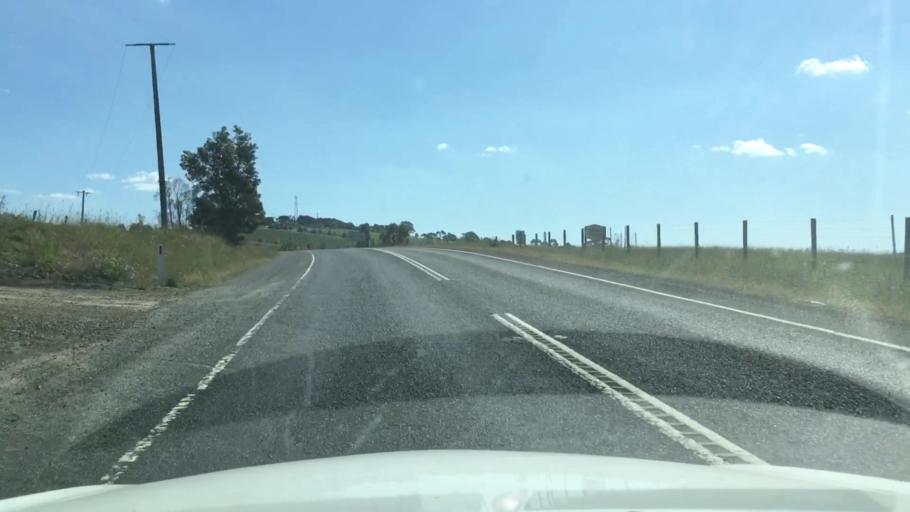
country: AU
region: Victoria
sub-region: Nillumbik
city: North Warrandyte
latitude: -37.6832
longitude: 145.2373
